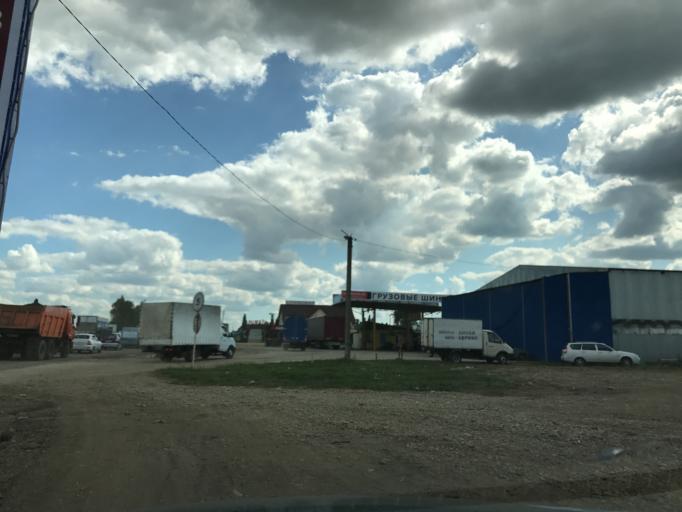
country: RU
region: Adygeya
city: Tlyustenkhabl'
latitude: 44.9651
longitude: 39.1171
